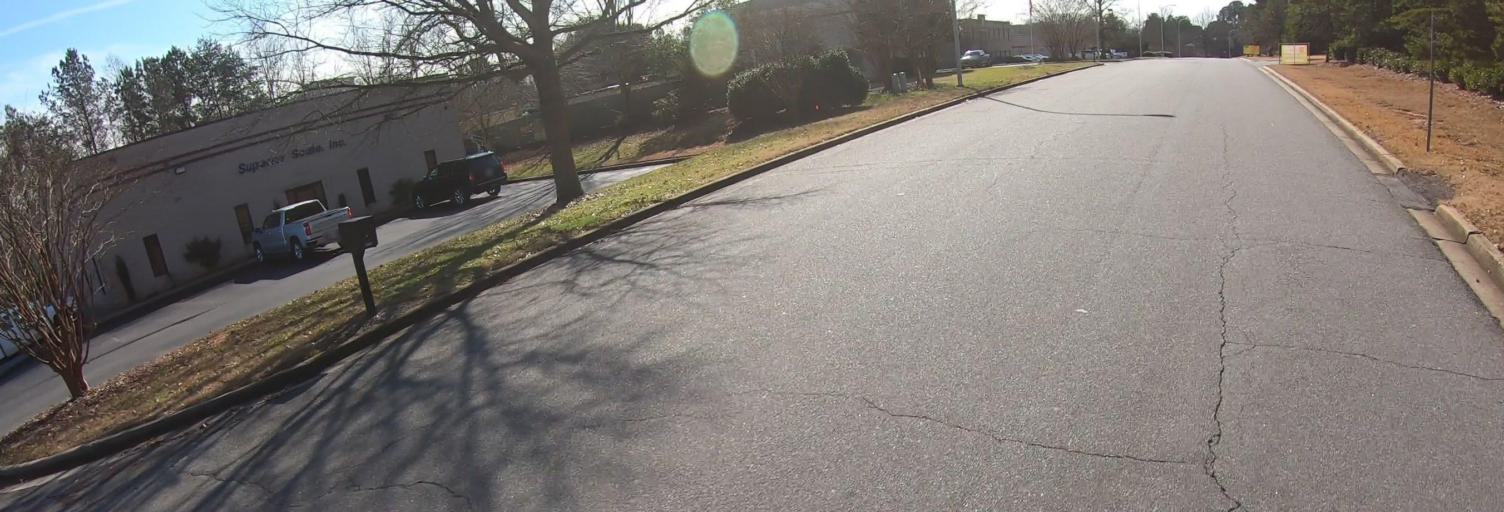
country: US
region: South Carolina
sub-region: York County
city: Fort Mill
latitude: 35.0361
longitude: -80.9636
